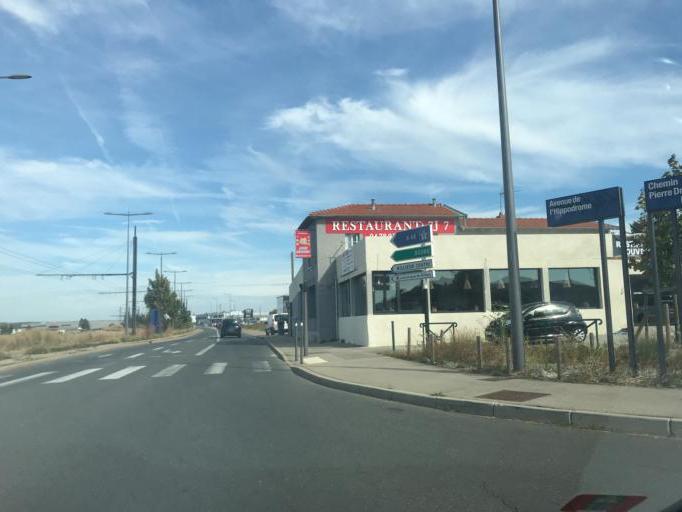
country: FR
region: Rhone-Alpes
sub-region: Departement du Rhone
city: Sathonay-Camp
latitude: 45.8084
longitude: 4.8713
